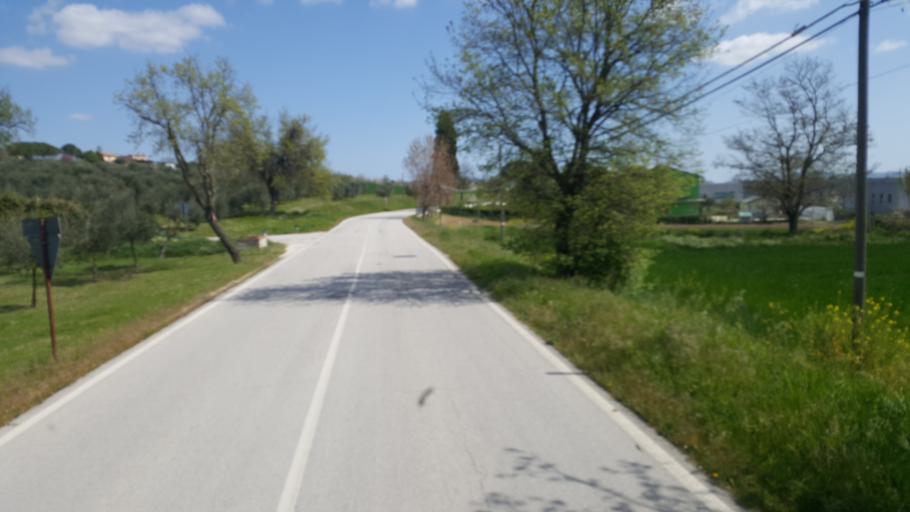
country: IT
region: The Marches
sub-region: Provincia di Macerata
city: Montecassiano
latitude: 43.3545
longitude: 13.4506
